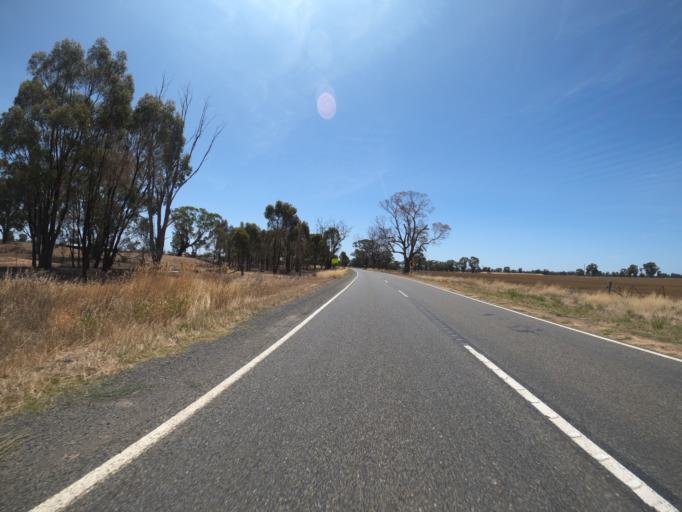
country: AU
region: Victoria
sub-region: Moira
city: Yarrawonga
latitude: -36.1900
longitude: 145.9672
